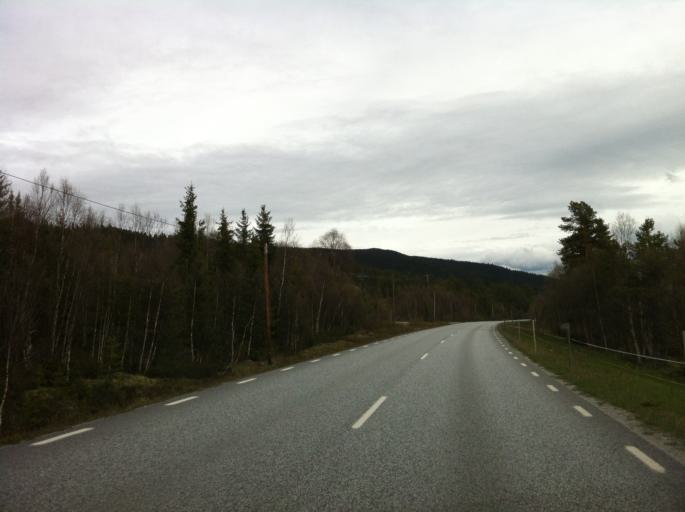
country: NO
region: Sor-Trondelag
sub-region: Tydal
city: Aas
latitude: 62.6149
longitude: 12.4915
